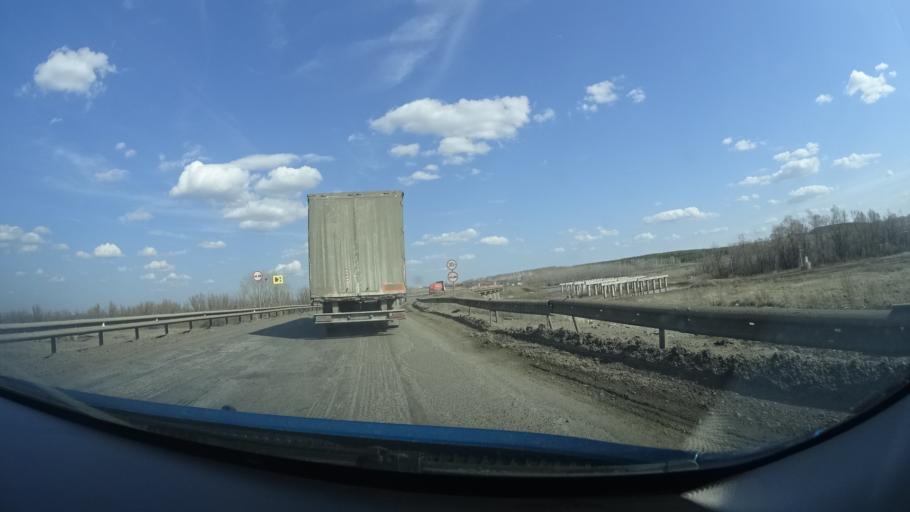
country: RU
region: Bashkortostan
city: Buzdyak
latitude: 54.6602
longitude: 54.6665
